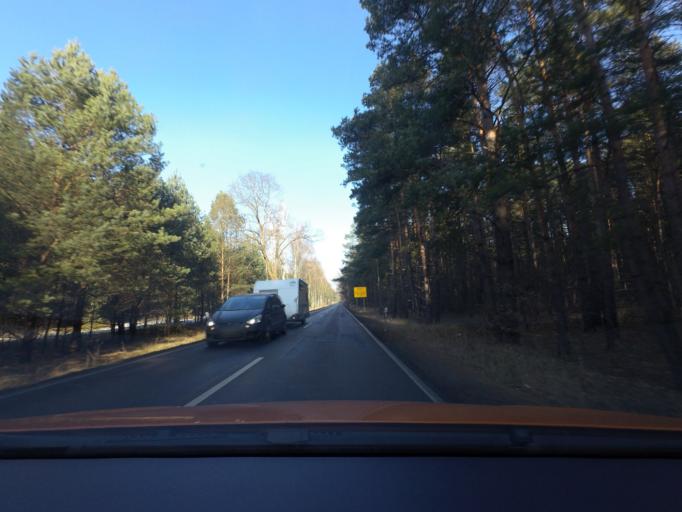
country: DE
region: Brandenburg
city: Birkenwerder
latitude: 52.7175
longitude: 13.3671
